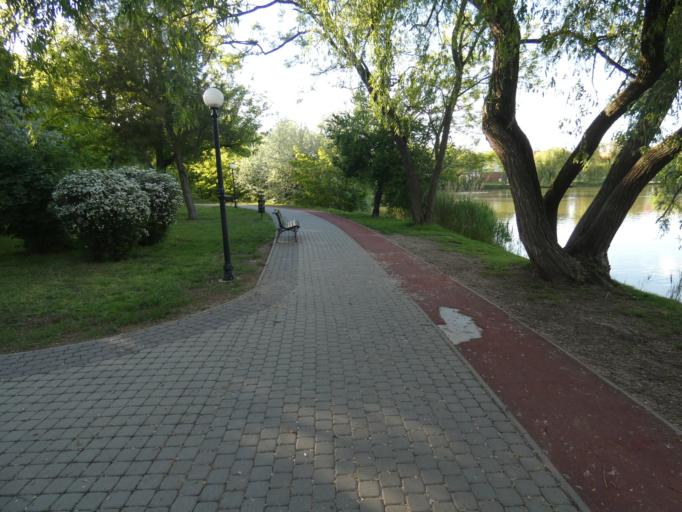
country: HU
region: Szabolcs-Szatmar-Bereg
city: Kotaj
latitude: 48.0044
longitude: 21.7266
